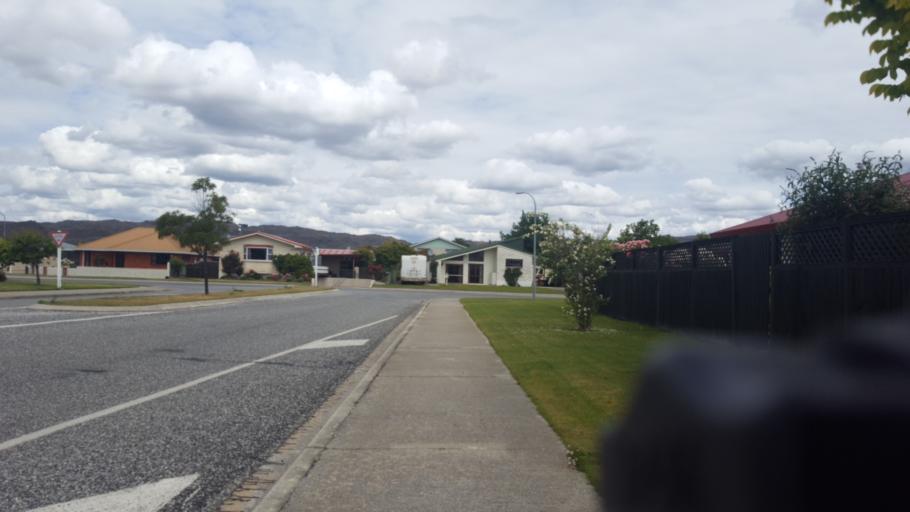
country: NZ
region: Otago
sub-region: Queenstown-Lakes District
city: Wanaka
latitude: -45.2448
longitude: 169.3772
